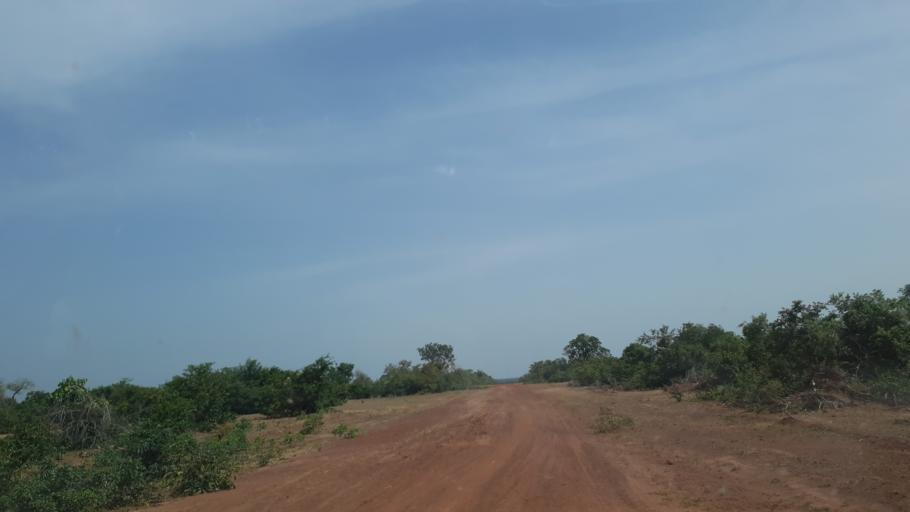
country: ML
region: Koulikoro
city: Dioila
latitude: 12.4625
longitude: -6.1910
